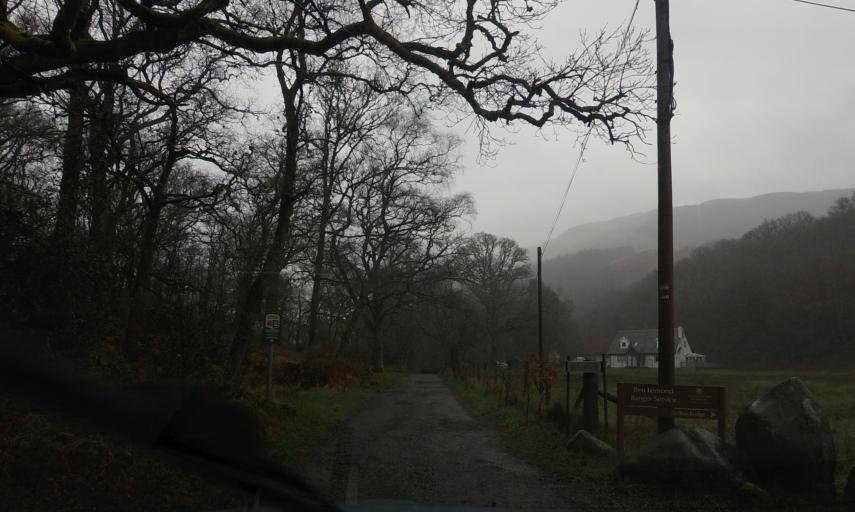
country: GB
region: Scotland
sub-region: West Dunbartonshire
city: Balloch
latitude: 56.1587
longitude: -4.6416
